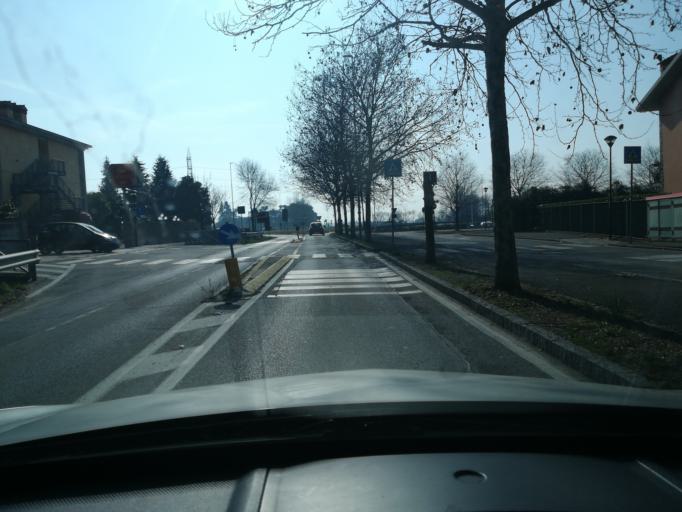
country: IT
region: Lombardy
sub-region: Provincia di Bergamo
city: Stezzano
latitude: 45.6433
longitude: 9.6563
